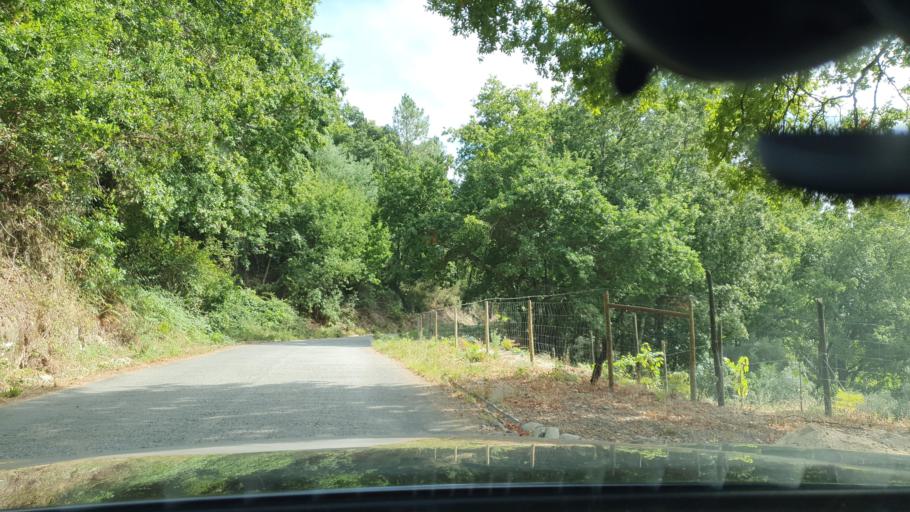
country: PT
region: Braga
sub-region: Vieira do Minho
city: Vieira do Minho
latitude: 41.6943
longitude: -8.0891
